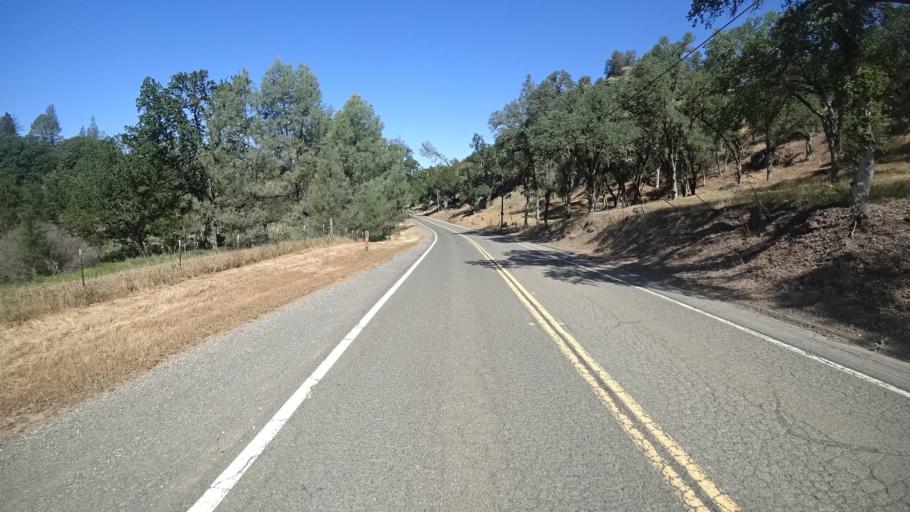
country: US
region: California
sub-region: Lake County
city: Lower Lake
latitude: 38.9018
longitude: -122.5717
